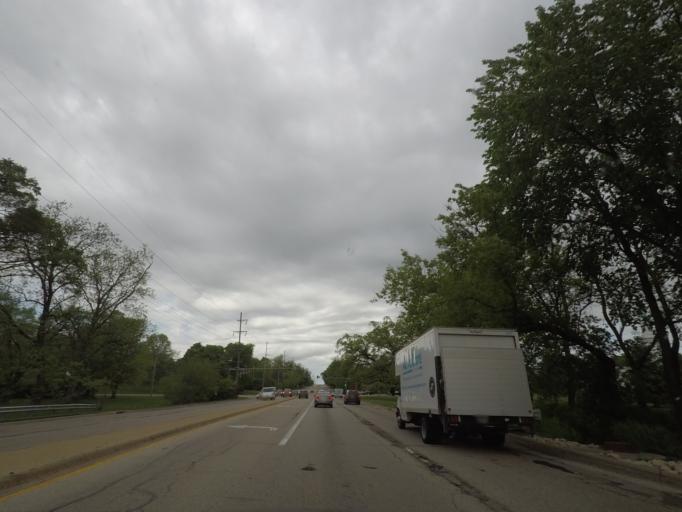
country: US
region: Illinois
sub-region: Winnebago County
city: Loves Park
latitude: 42.2948
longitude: -89.0290
